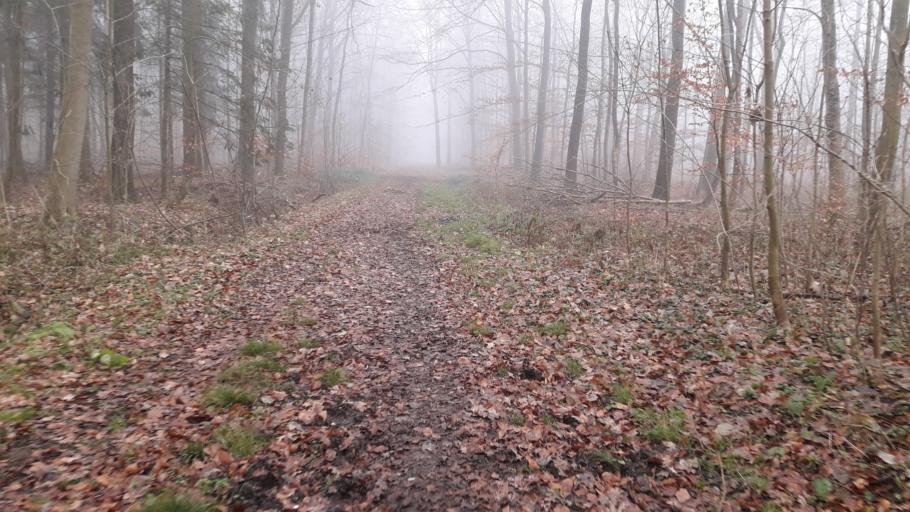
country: DE
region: Schleswig-Holstein
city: Quickborn
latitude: 53.7176
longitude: 9.8767
